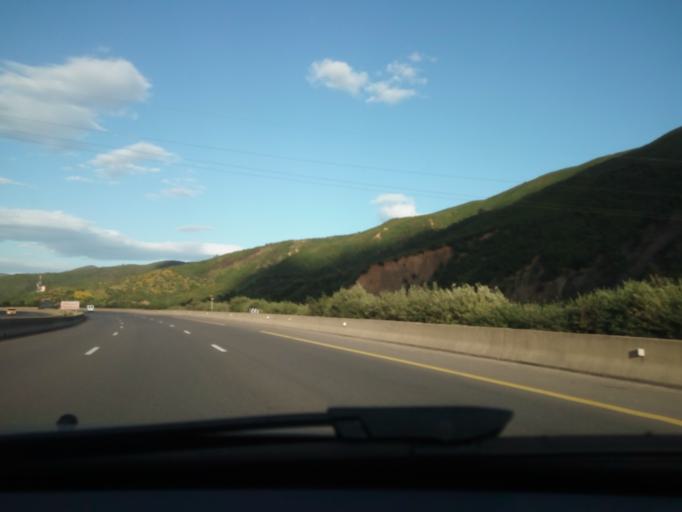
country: DZ
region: Tipaza
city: El Affroun
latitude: 36.3910
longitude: 2.5202
